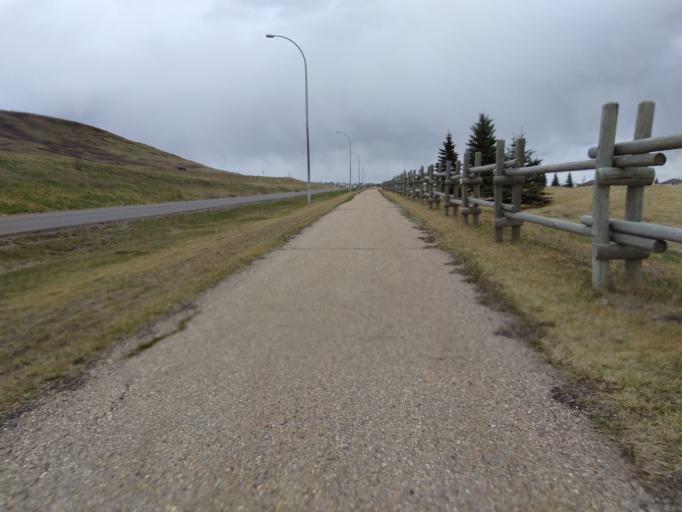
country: CA
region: Alberta
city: Cochrane
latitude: 51.1906
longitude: -114.4485
